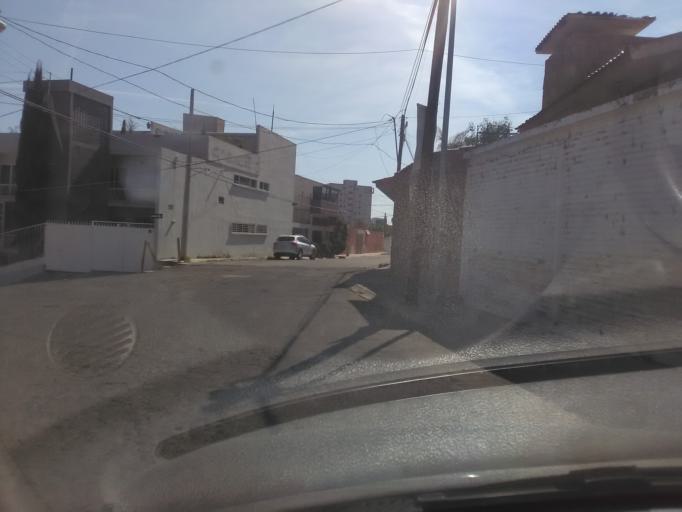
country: MX
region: Durango
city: Victoria de Durango
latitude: 24.0242
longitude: -104.6824
